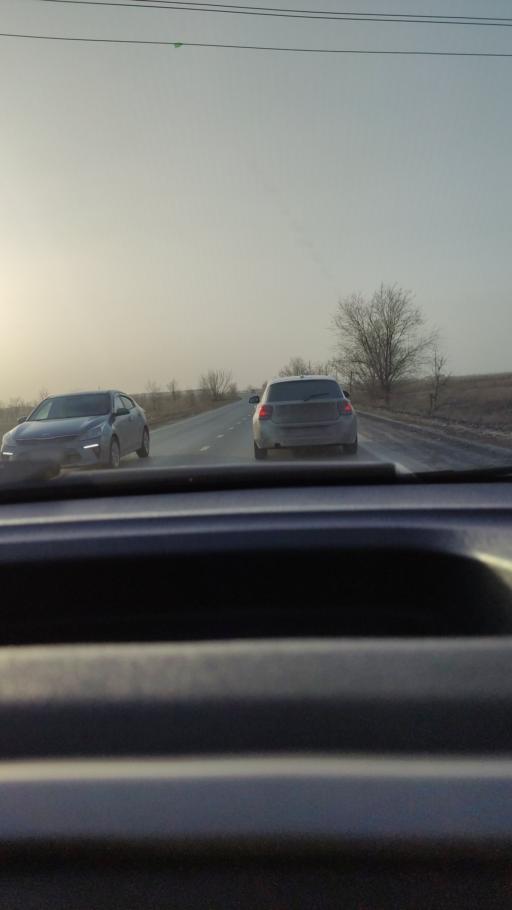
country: RU
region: Samara
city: Podstepki
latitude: 53.5176
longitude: 49.2114
